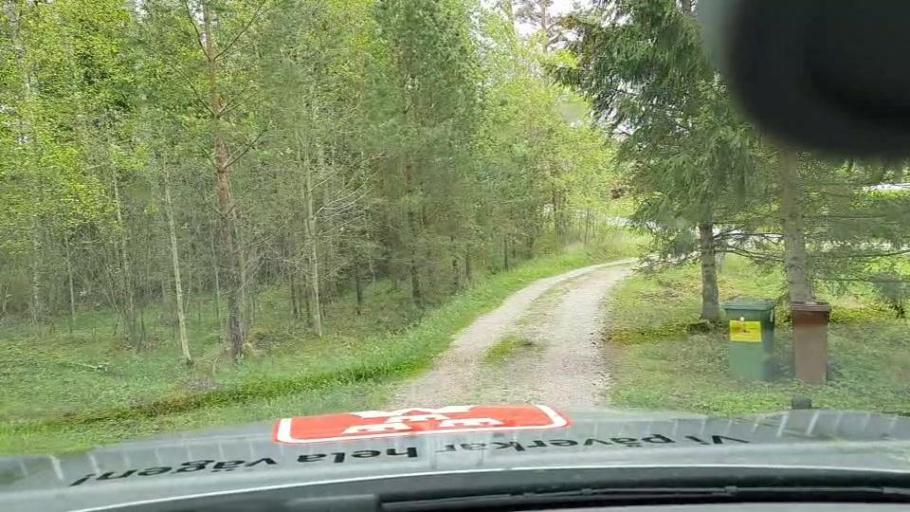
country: SE
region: Soedermanland
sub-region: Nykopings Kommun
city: Svalsta
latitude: 58.6188
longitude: 16.9407
